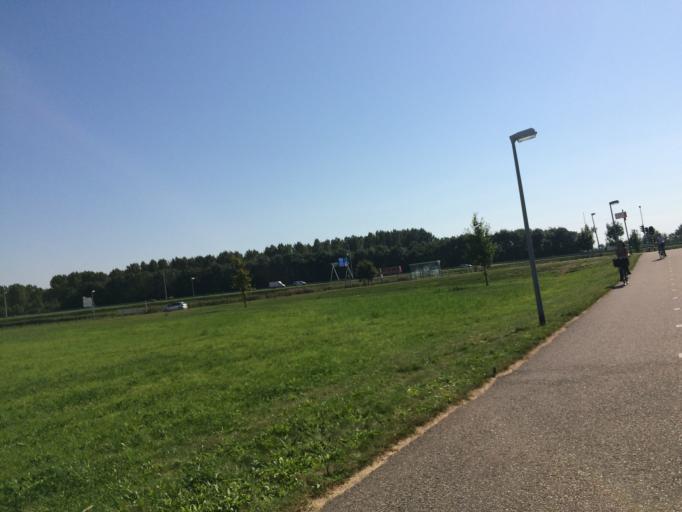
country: NL
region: Flevoland
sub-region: Gemeente Almere
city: Almere Stad
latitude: 52.3547
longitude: 5.2440
